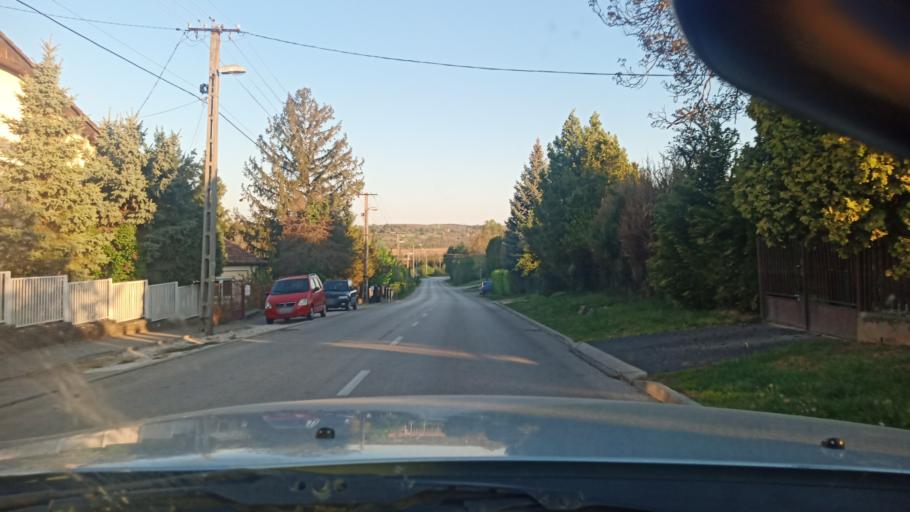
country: HU
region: Zala
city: Heviz
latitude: 46.7903
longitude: 17.1787
